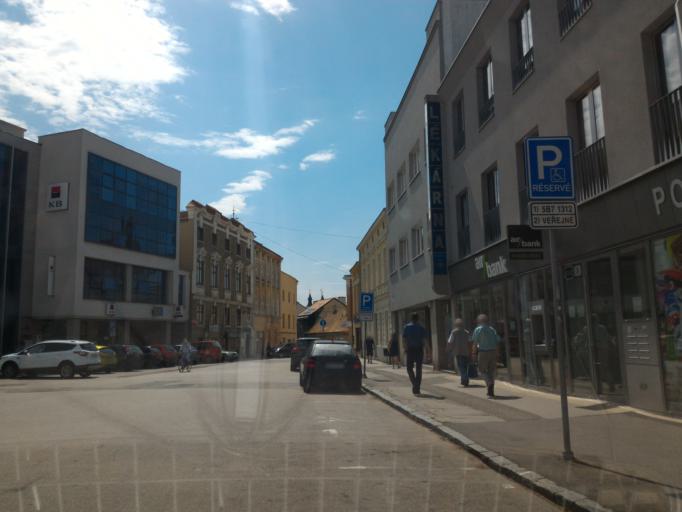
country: CZ
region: South Moravian
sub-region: Okres Znojmo
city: Znojmo
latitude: 48.8593
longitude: 16.0478
